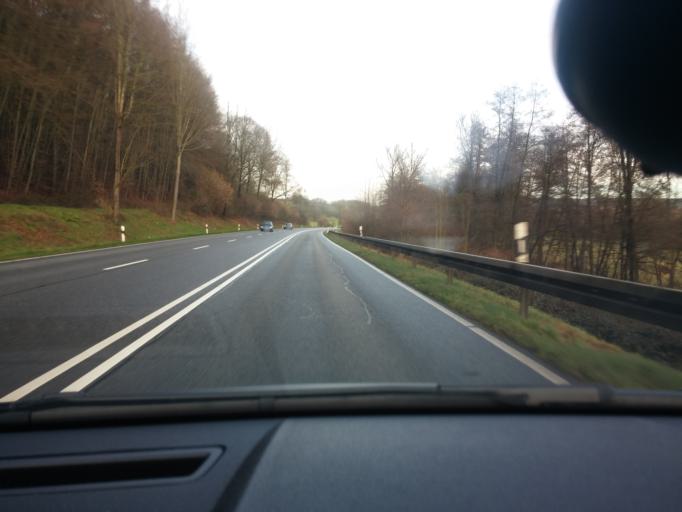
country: DE
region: Hesse
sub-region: Regierungsbezirk Darmstadt
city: Bad Konig
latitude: 49.7388
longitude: 8.9936
